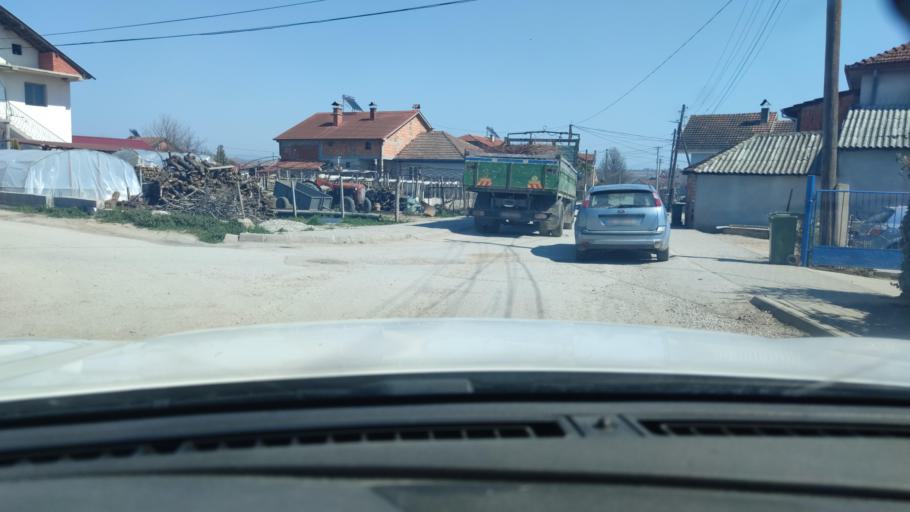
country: MK
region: Rosoman
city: Rosoman
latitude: 41.5163
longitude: 21.9394
